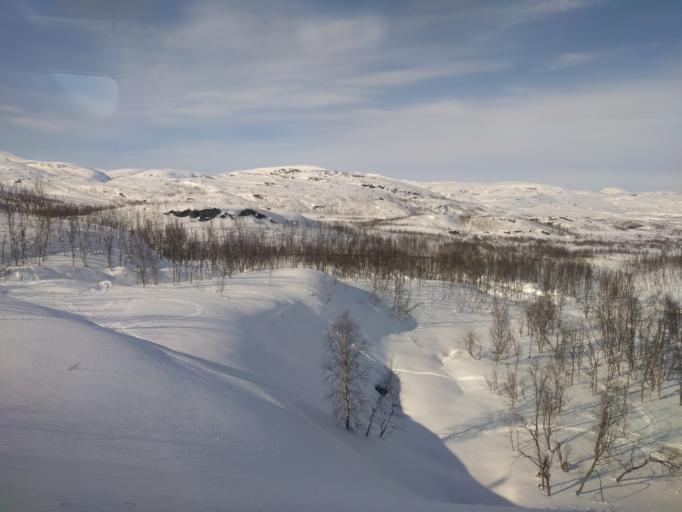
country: NO
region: Troms
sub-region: Bardu
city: Setermoen
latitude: 68.4215
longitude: 18.2972
